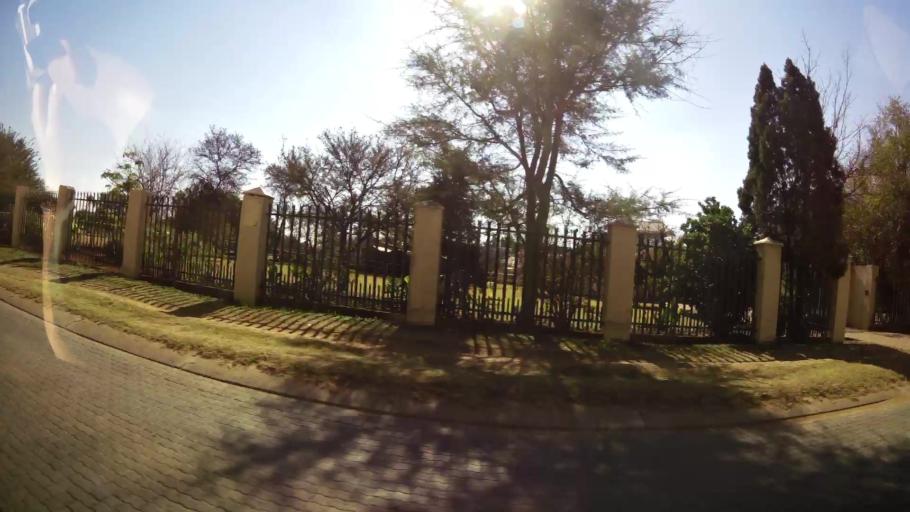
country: ZA
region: Gauteng
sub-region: City of Tshwane Metropolitan Municipality
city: Pretoria
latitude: -25.6572
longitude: 28.2628
